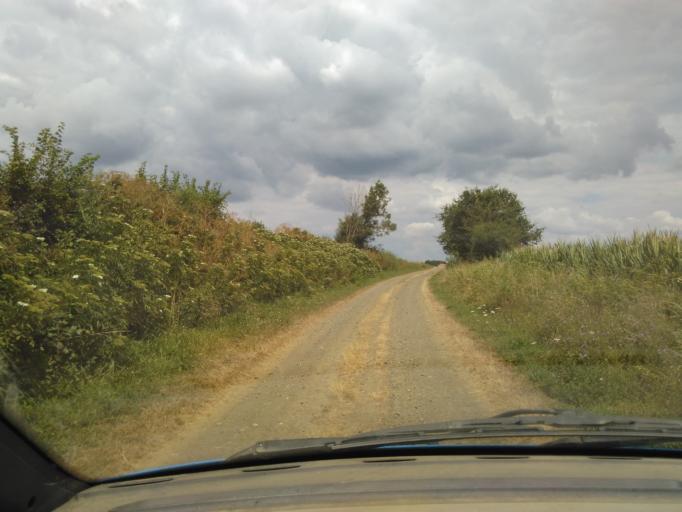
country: FR
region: Pays de la Loire
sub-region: Departement de la Vendee
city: Sainte-Hermine
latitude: 46.5708
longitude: -1.0249
